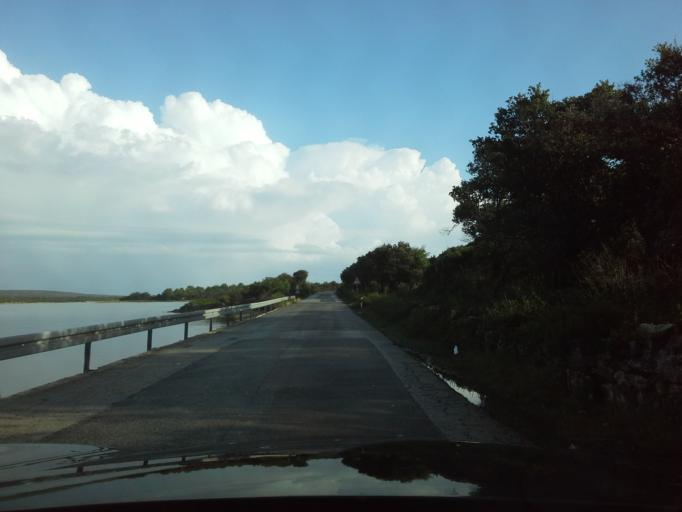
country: HR
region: Primorsko-Goranska
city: Mali Losinj
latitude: 44.6885
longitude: 14.3925
